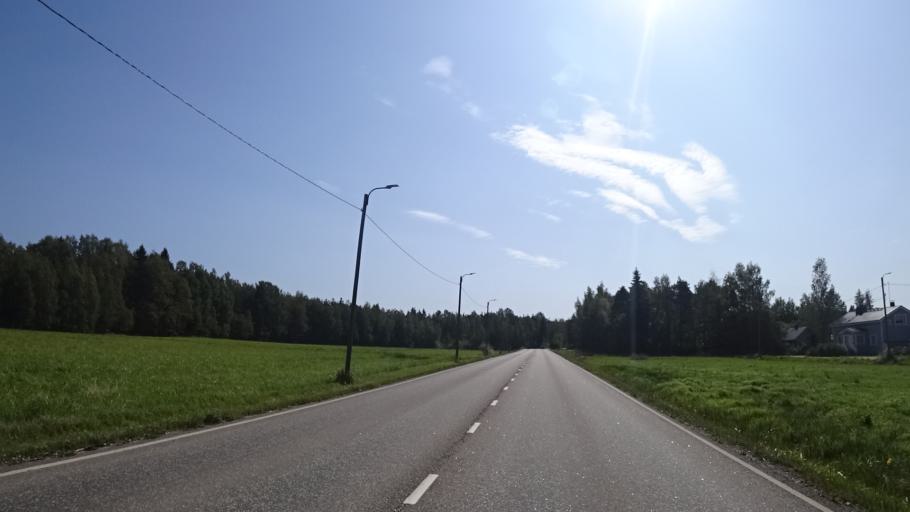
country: FI
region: Kymenlaakso
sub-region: Kotka-Hamina
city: Karhula
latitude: 60.5127
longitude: 26.9618
